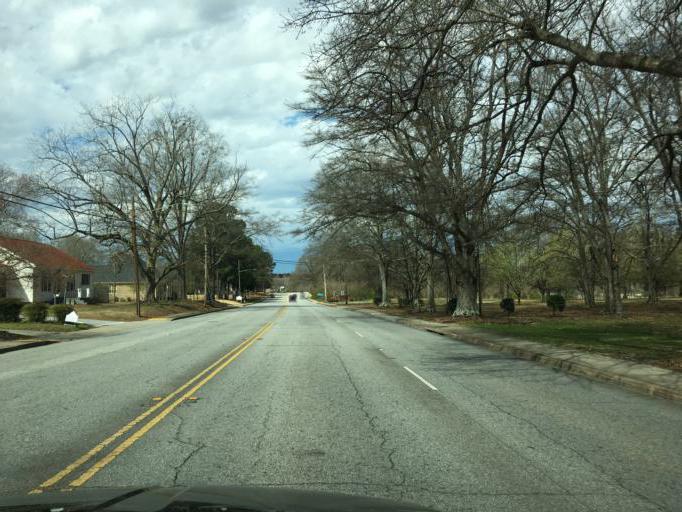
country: US
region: South Carolina
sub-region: Greenville County
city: Fountain Inn
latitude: 34.6993
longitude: -82.2091
